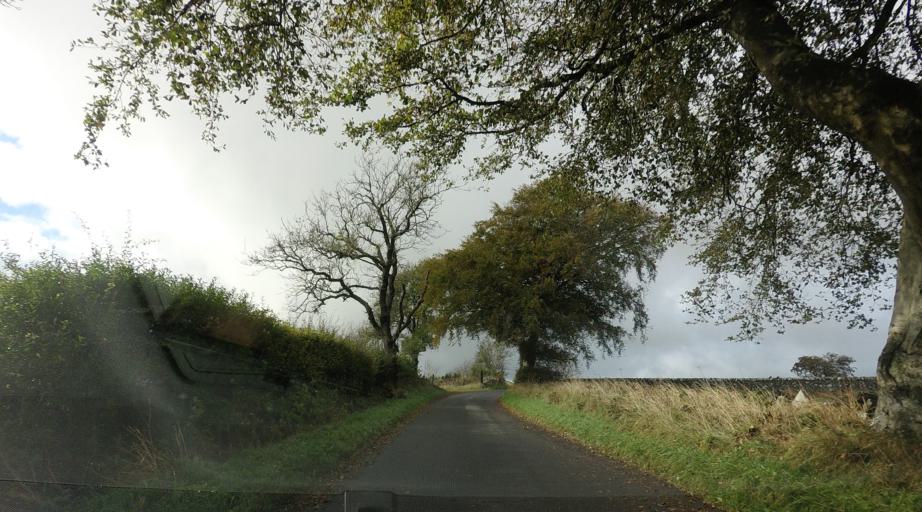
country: GB
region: Scotland
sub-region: Fife
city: Balmullo
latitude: 56.3605
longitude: -2.9594
